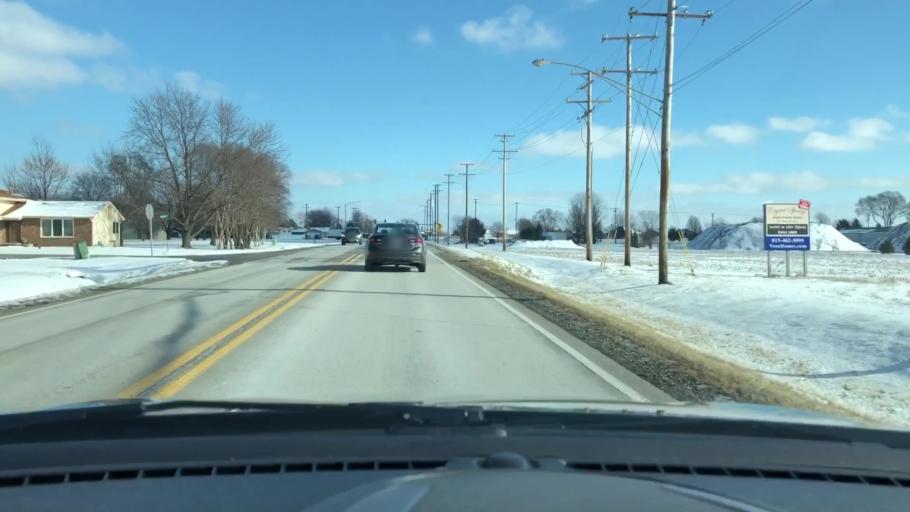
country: US
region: Illinois
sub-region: Will County
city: New Lenox
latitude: 41.4834
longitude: -87.9444
